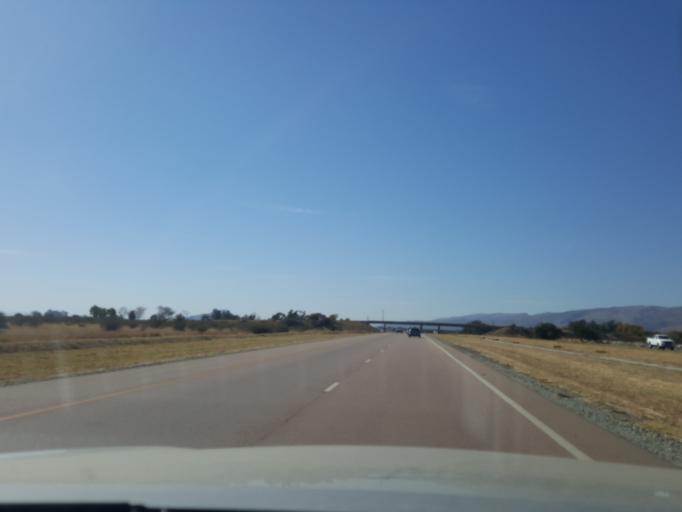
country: ZA
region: North-West
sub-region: Bojanala Platinum District Municipality
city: Brits
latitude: -25.7368
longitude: 27.6295
